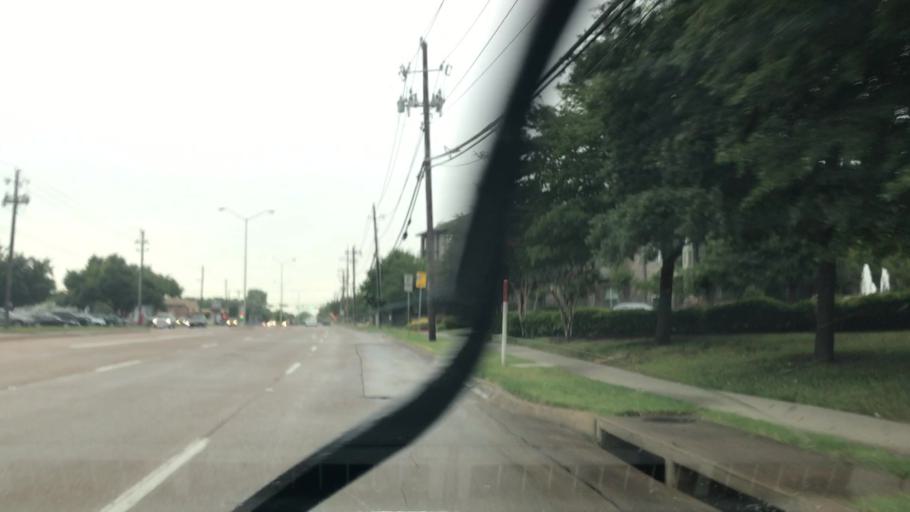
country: US
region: Texas
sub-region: Dallas County
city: Richardson
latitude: 32.9117
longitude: -96.7461
